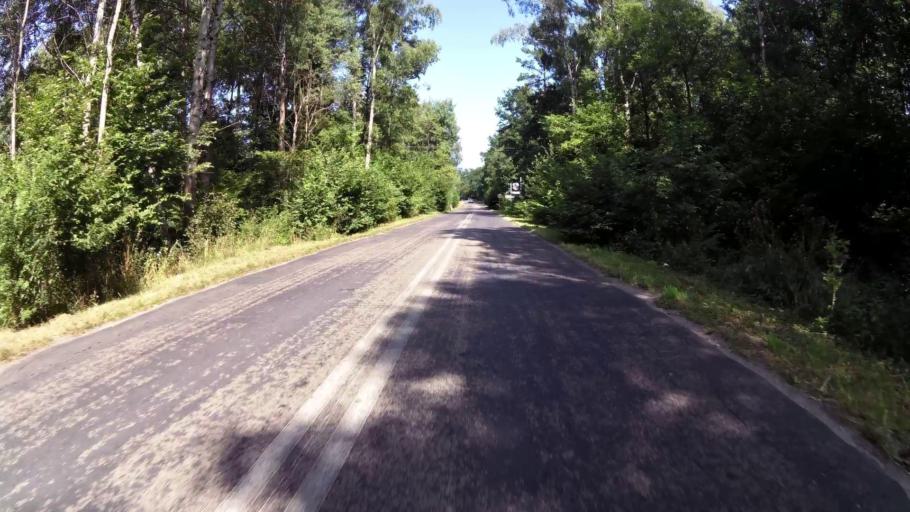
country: PL
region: West Pomeranian Voivodeship
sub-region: Powiat stargardzki
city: Dobrzany
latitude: 53.3201
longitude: 15.3847
